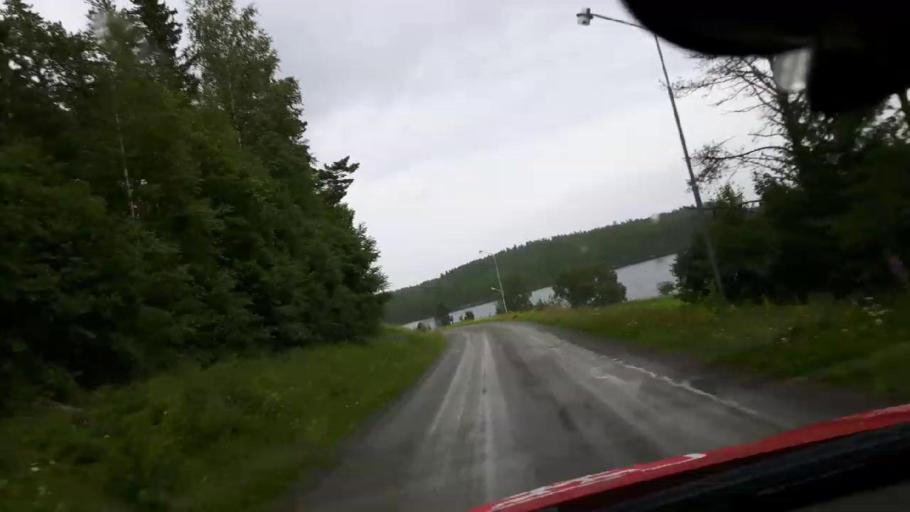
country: SE
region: Jaemtland
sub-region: OEstersunds Kommun
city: Brunflo
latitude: 62.9085
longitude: 14.8451
